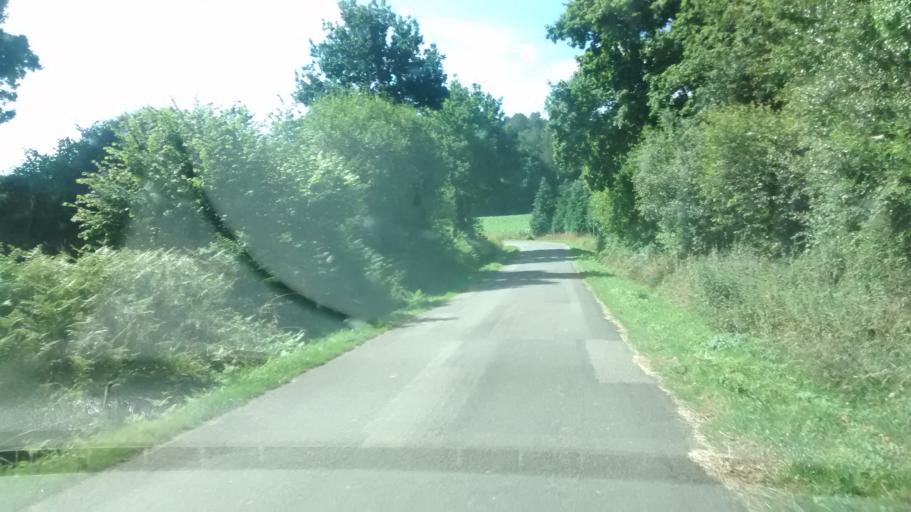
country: FR
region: Brittany
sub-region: Departement du Morbihan
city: Molac
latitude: 47.7176
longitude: -2.4599
